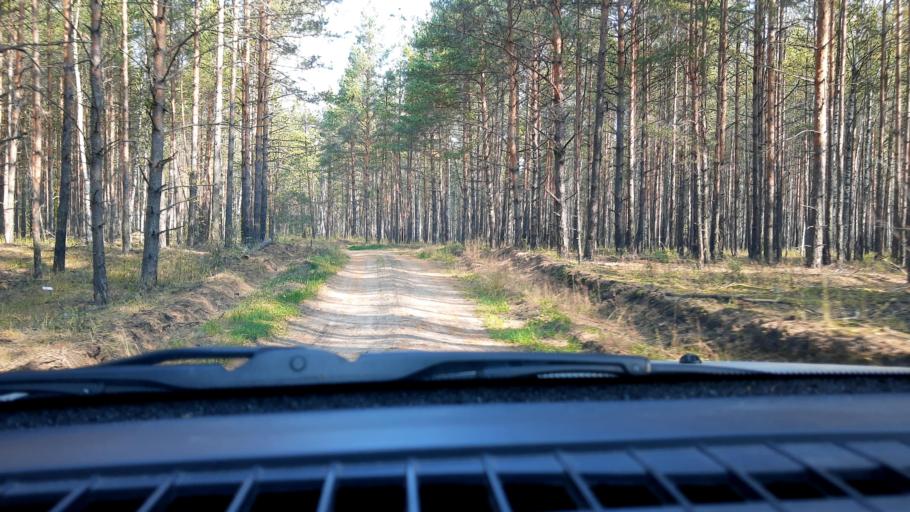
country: RU
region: Nizjnij Novgorod
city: Lukino
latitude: 56.3904
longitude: 43.6279
